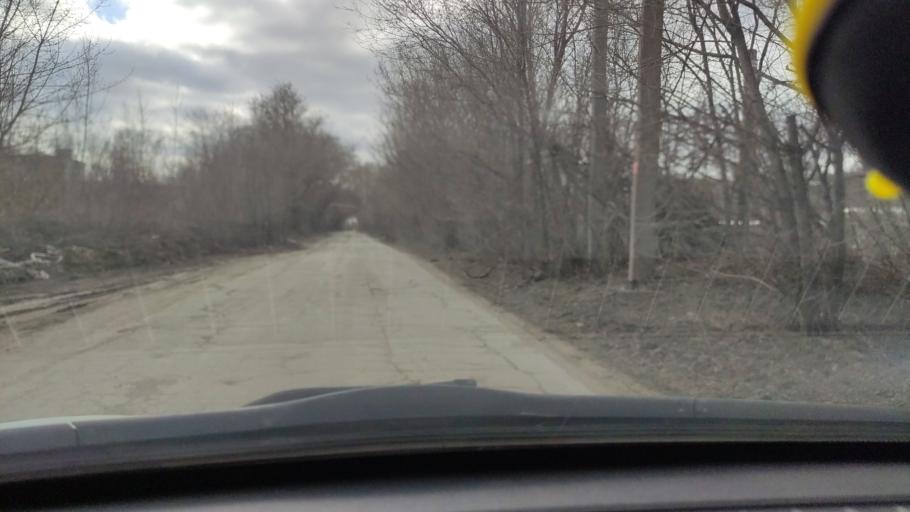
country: RU
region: Samara
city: Tol'yatti
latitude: 53.5213
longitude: 49.4547
